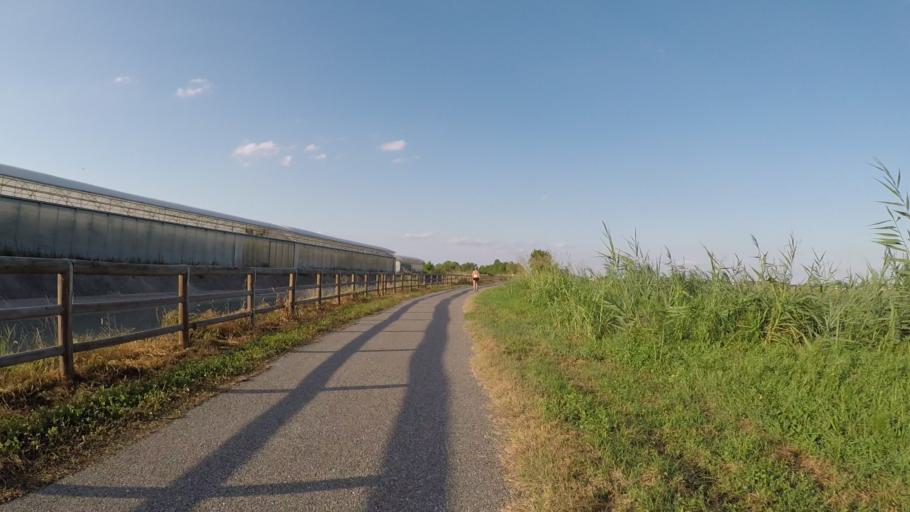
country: IT
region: Veneto
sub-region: Provincia di Rovigo
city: Lendinara
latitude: 45.0672
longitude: 11.6147
